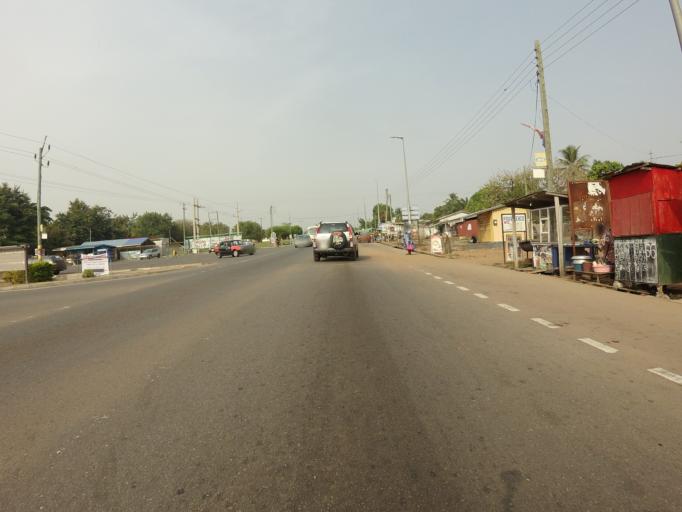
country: GH
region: Volta
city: Ho
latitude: 6.6033
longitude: 0.4850
